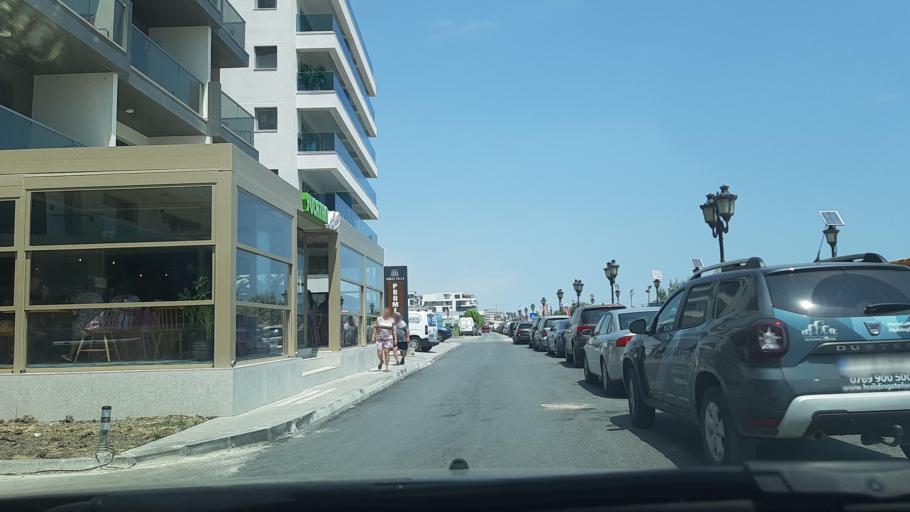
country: RO
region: Constanta
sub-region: Comuna Navodari
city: Navodari
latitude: 44.2944
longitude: 28.6243
